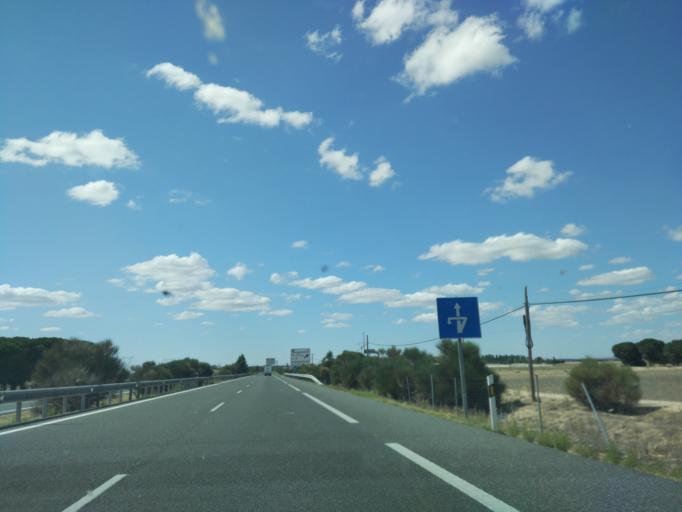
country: ES
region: Castille and Leon
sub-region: Provincia de Valladolid
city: San Vicente del Palacio
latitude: 41.2163
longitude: -4.8383
